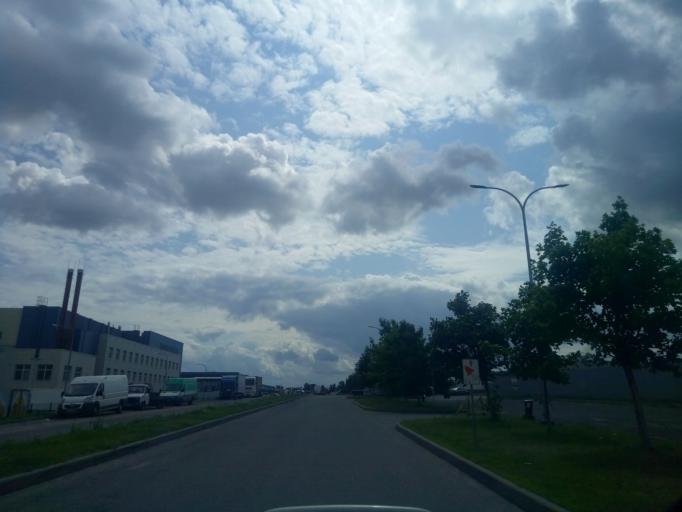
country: BY
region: Minsk
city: Zhdanovichy
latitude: 53.9372
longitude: 27.4231
